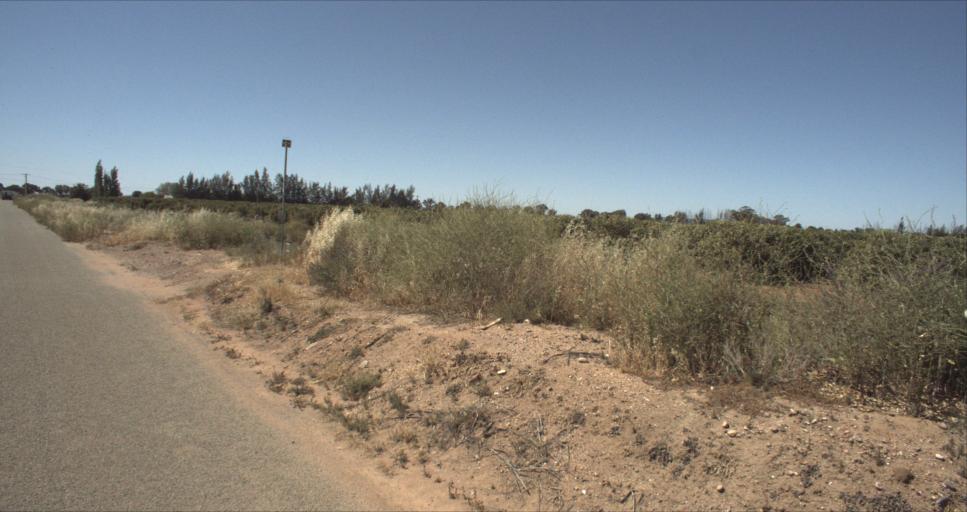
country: AU
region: New South Wales
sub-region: Leeton
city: Leeton
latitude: -34.5355
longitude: 146.3525
